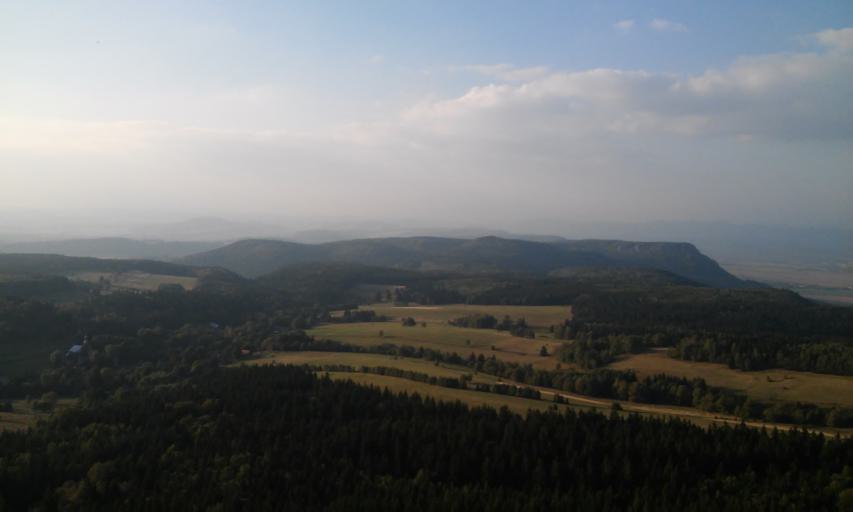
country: CZ
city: Machov
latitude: 50.4857
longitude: 16.3393
